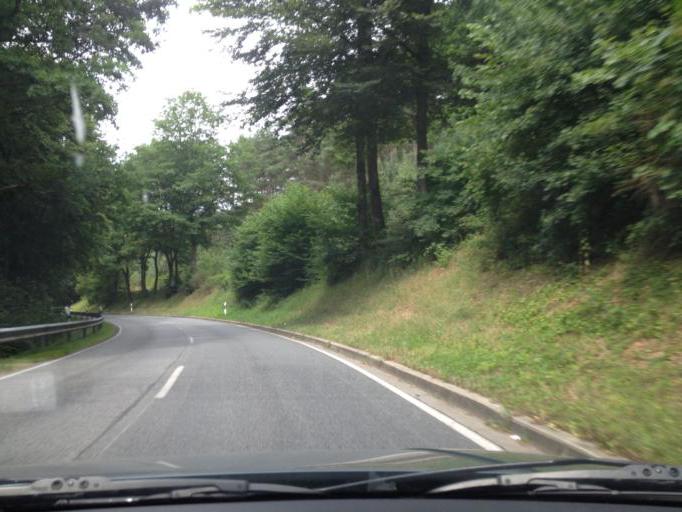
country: DE
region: Rheinland-Pfalz
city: Horbach
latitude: 49.3415
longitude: 7.6570
